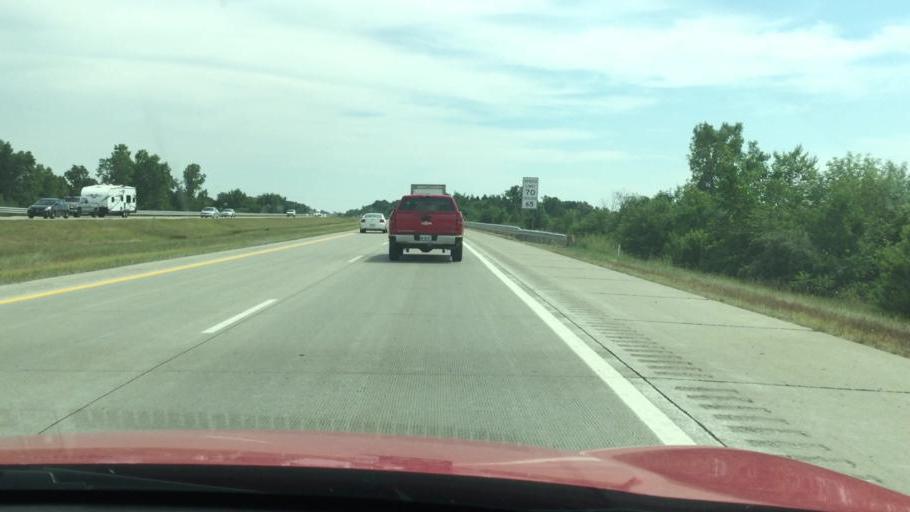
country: US
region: Michigan
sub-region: Genesee County
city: Flint
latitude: 42.9646
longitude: -83.6829
